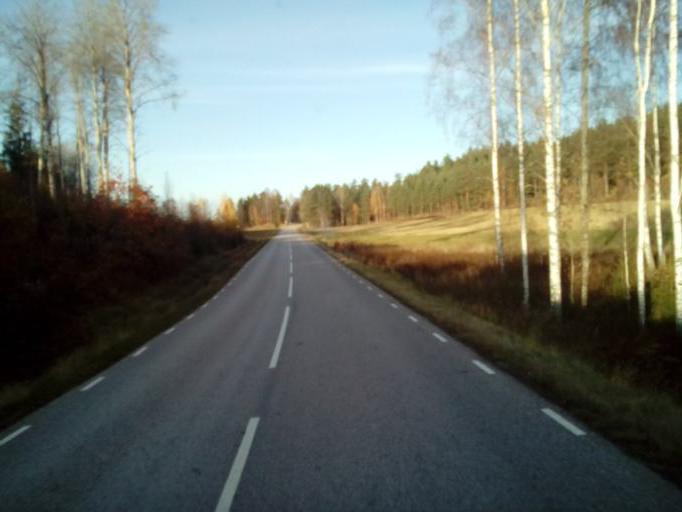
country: SE
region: Kalmar
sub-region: Vasterviks Kommun
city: Ankarsrum
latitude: 57.7789
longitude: 16.1641
